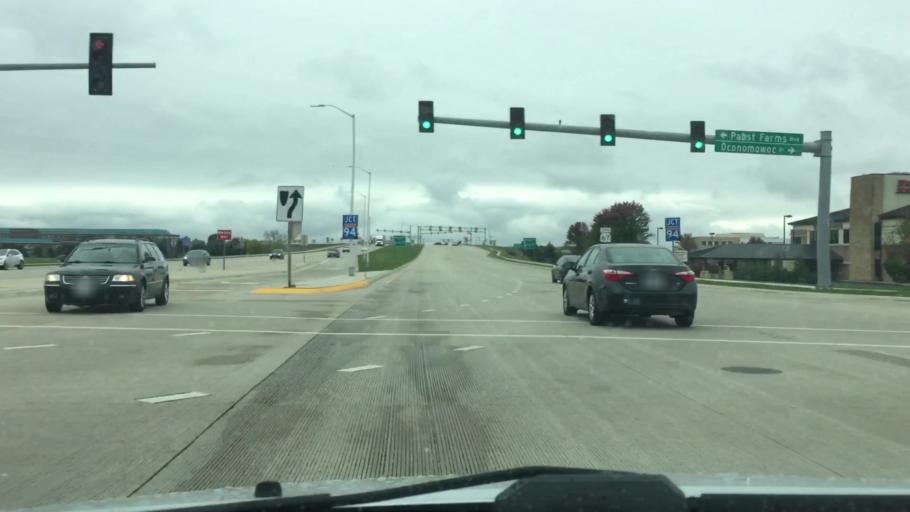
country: US
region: Wisconsin
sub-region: Waukesha County
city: Oconomowoc
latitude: 43.0739
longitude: -88.4710
